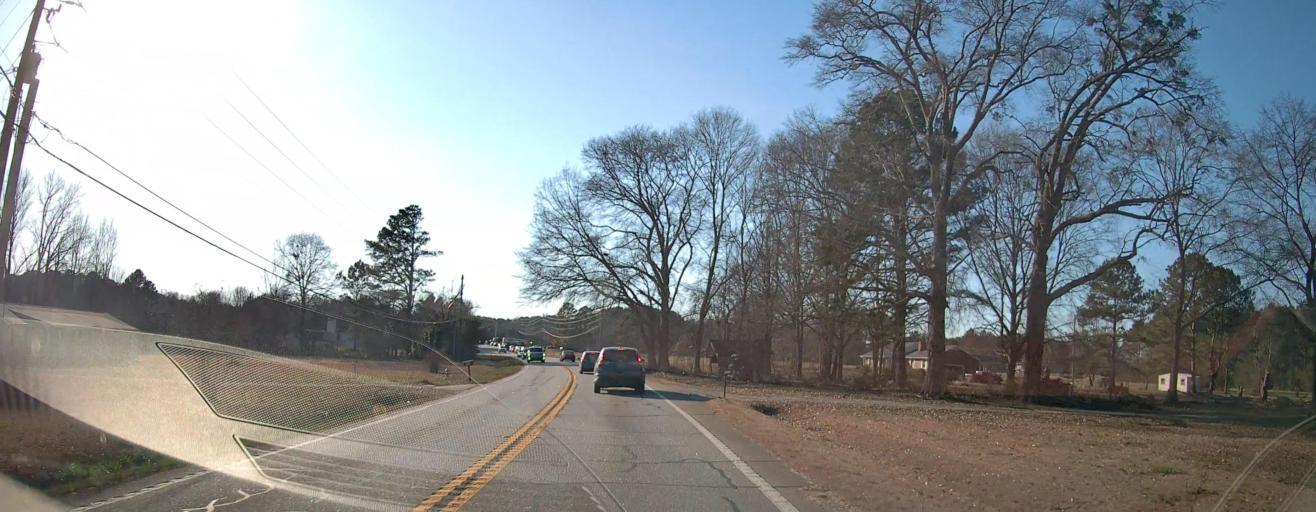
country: US
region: Georgia
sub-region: Henry County
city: McDonough
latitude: 33.4323
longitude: -84.2030
